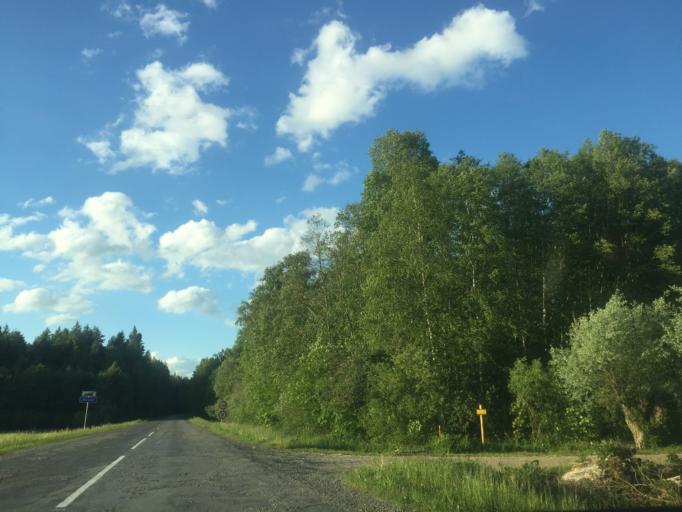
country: LV
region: Kandava
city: Kandava
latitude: 57.0016
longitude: 22.7775
